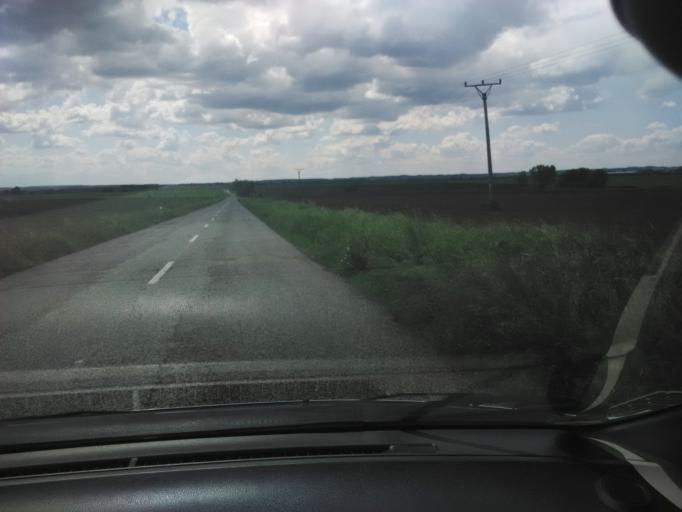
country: SK
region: Nitriansky
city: Levice
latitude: 48.1534
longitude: 18.5388
